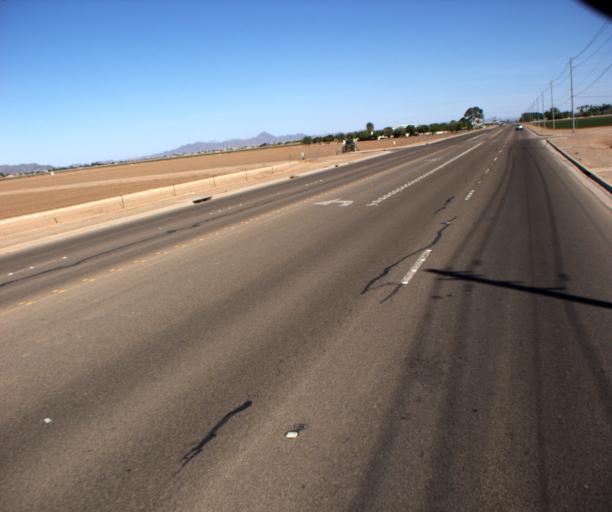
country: US
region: Arizona
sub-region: Yuma County
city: Yuma
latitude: 32.6540
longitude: -114.6500
